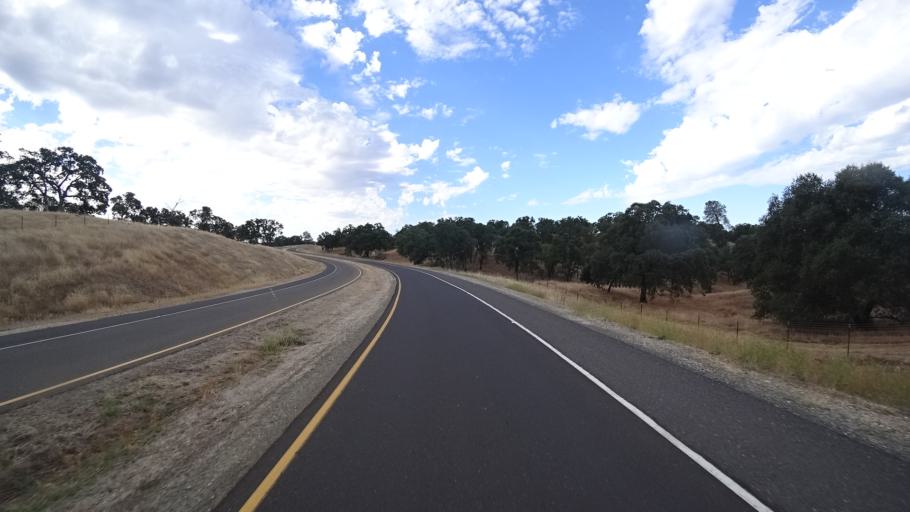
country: US
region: California
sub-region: Calaveras County
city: Copperopolis
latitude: 37.9608
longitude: -120.6533
